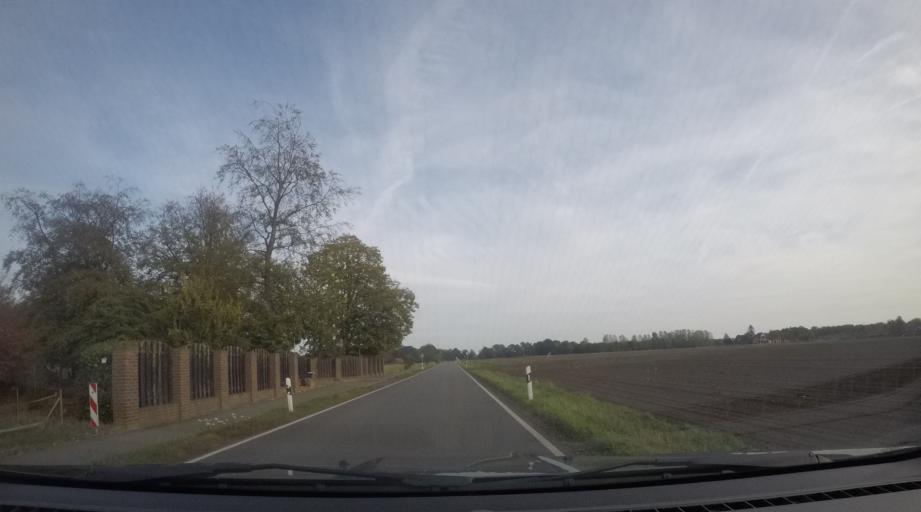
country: DE
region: North Rhine-Westphalia
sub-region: Regierungsbezirk Dusseldorf
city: Bocholt
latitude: 51.8155
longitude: 6.6424
